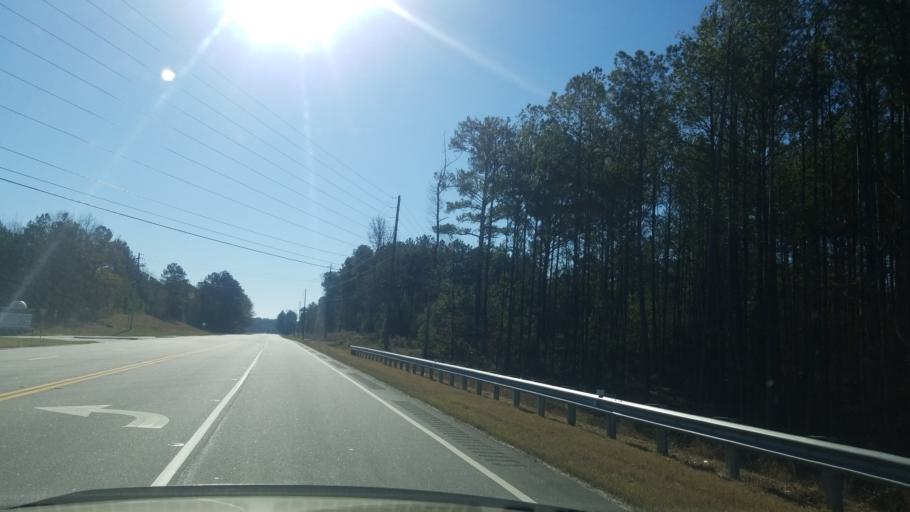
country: US
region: Georgia
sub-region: Troup County
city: West Point
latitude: 32.8548
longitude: -85.1304
